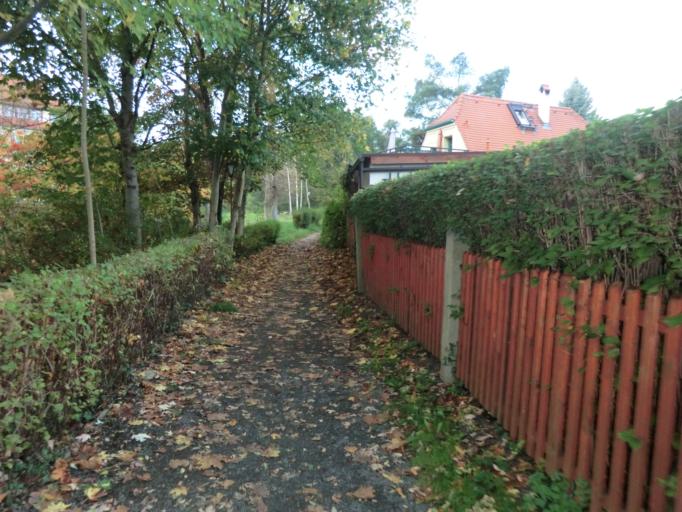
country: DE
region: Saxony
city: Albertstadt
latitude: 51.1073
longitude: 13.7607
